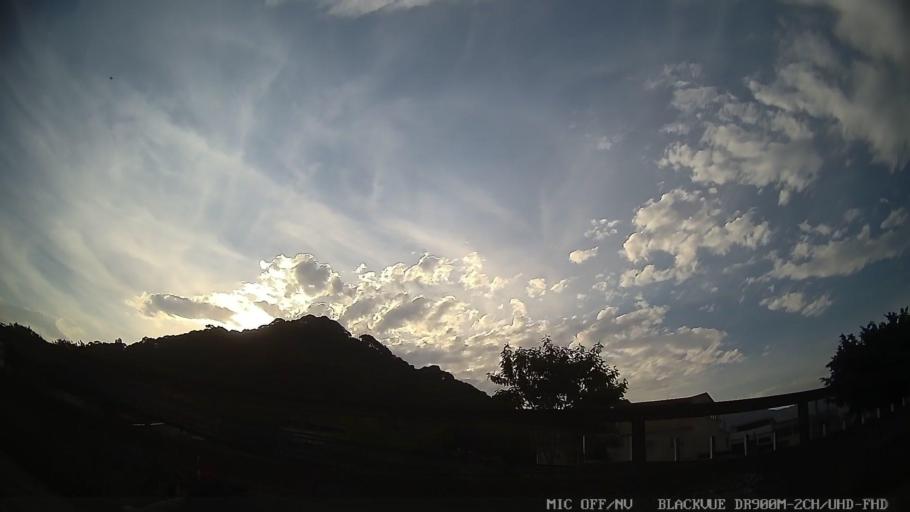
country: BR
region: Sao Paulo
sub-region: Cubatao
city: Cubatao
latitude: -23.8981
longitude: -46.4348
